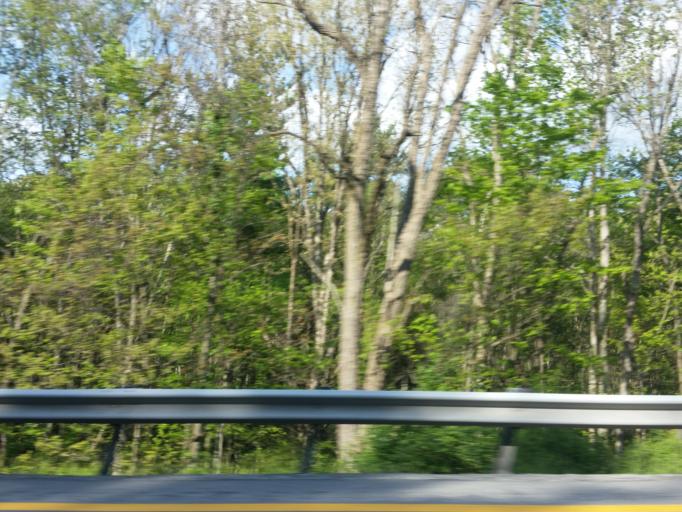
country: US
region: West Virginia
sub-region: Raleigh County
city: Shady Spring
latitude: 37.6803
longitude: -81.1241
